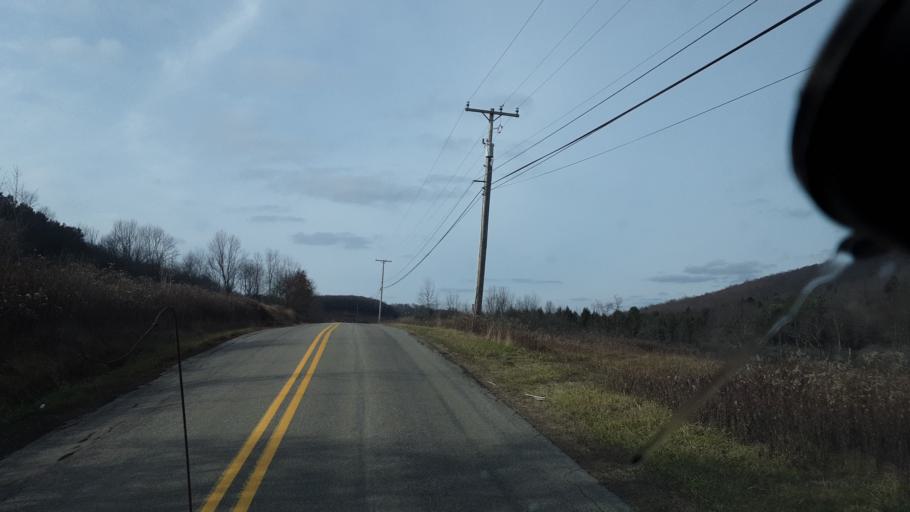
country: US
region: New York
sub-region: Allegany County
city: Andover
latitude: 41.9256
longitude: -77.7901
